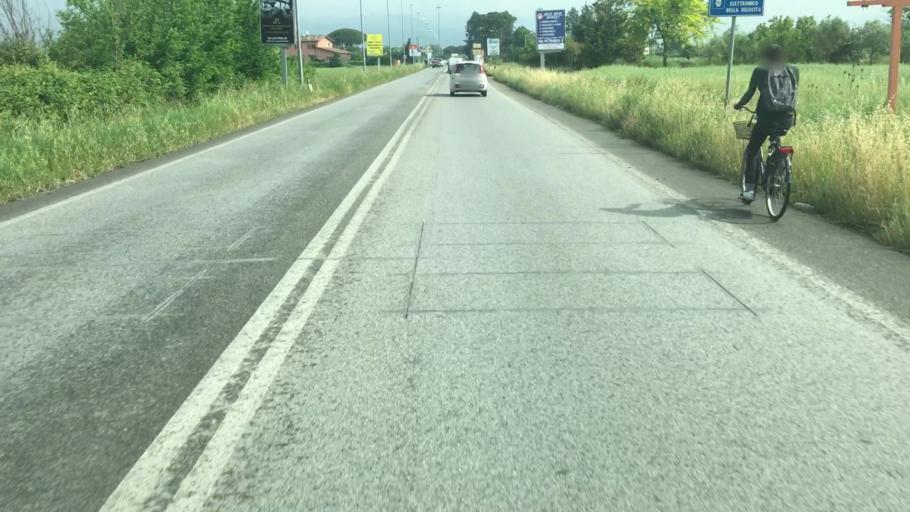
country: IT
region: Tuscany
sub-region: Province of Florence
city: San Mauro
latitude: 43.8105
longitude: 11.1186
